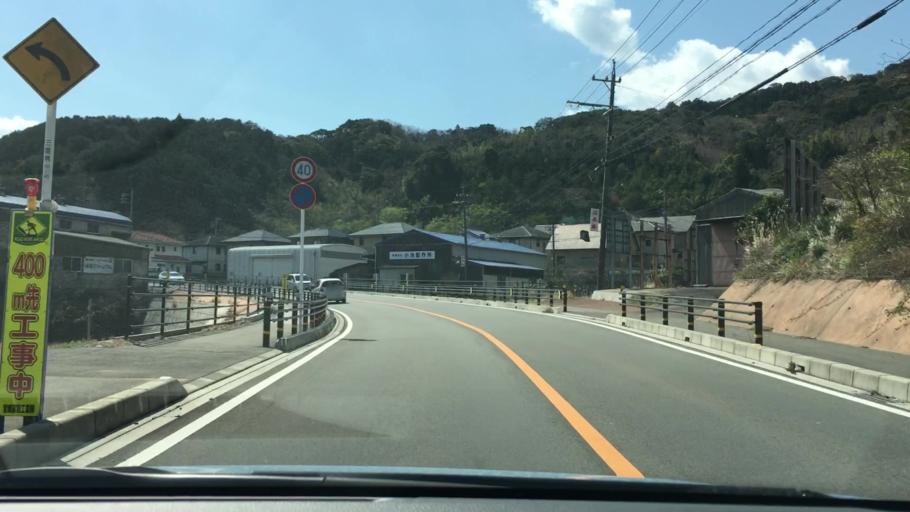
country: JP
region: Mie
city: Toba
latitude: 34.4643
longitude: 136.8549
